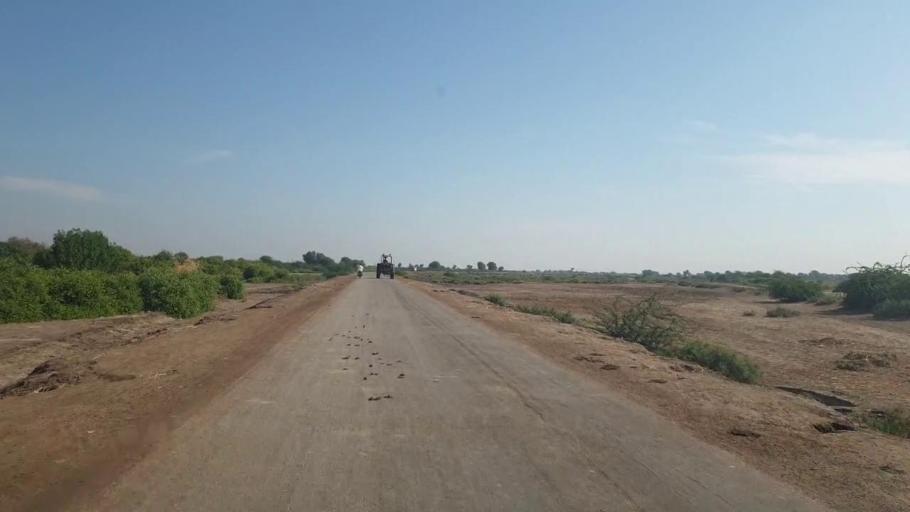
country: PK
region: Sindh
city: Rajo Khanani
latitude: 24.9224
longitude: 68.9317
